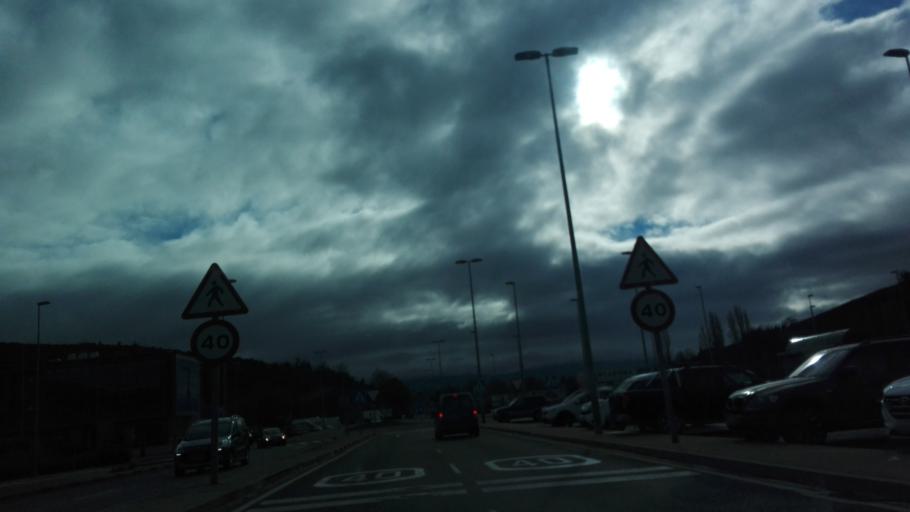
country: ES
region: Navarre
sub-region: Provincia de Navarra
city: Egues-Uharte
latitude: 42.8365
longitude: -1.5864
